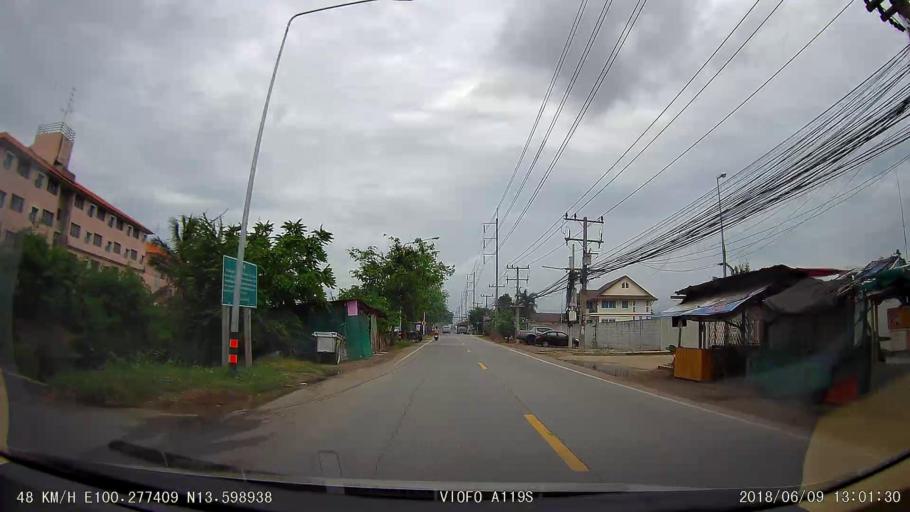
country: TH
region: Samut Sakhon
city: Samut Sakhon
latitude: 13.5989
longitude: 100.2774
